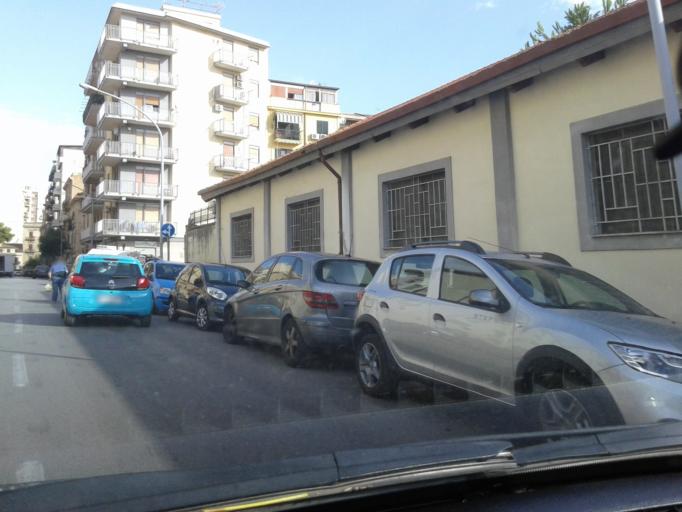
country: IT
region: Sicily
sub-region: Palermo
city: Palermo
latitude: 38.1043
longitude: 13.3400
